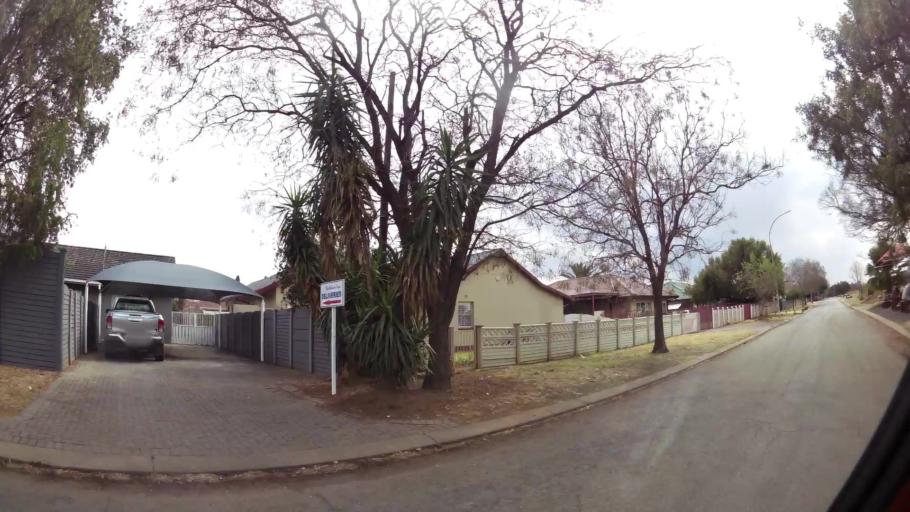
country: ZA
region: Gauteng
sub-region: Sedibeng District Municipality
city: Vanderbijlpark
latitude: -26.7241
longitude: 27.8546
